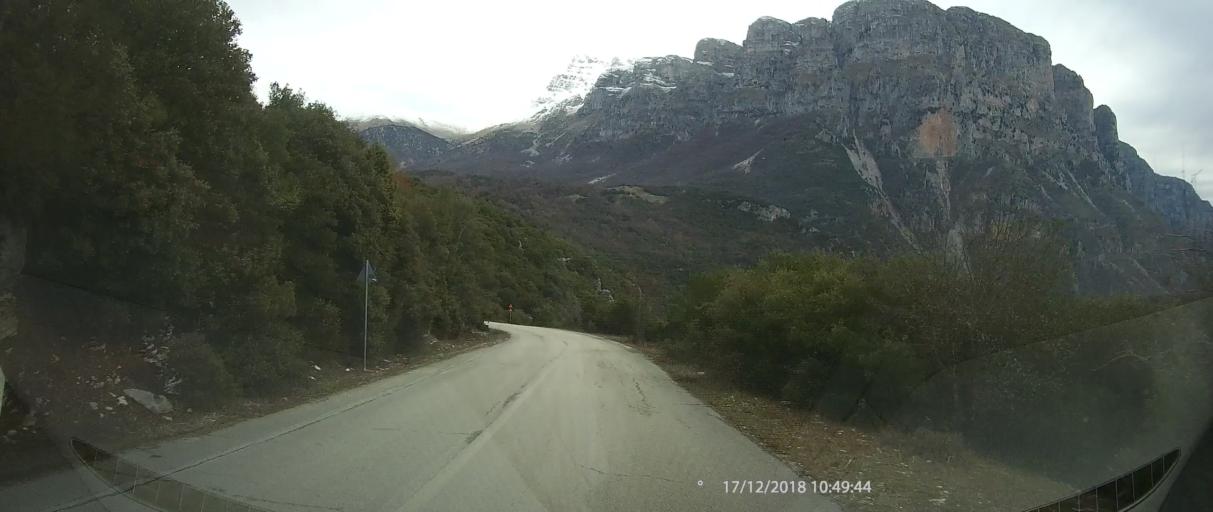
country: GR
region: Epirus
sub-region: Nomos Ioanninon
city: Kalpaki
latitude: 39.9596
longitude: 20.6989
